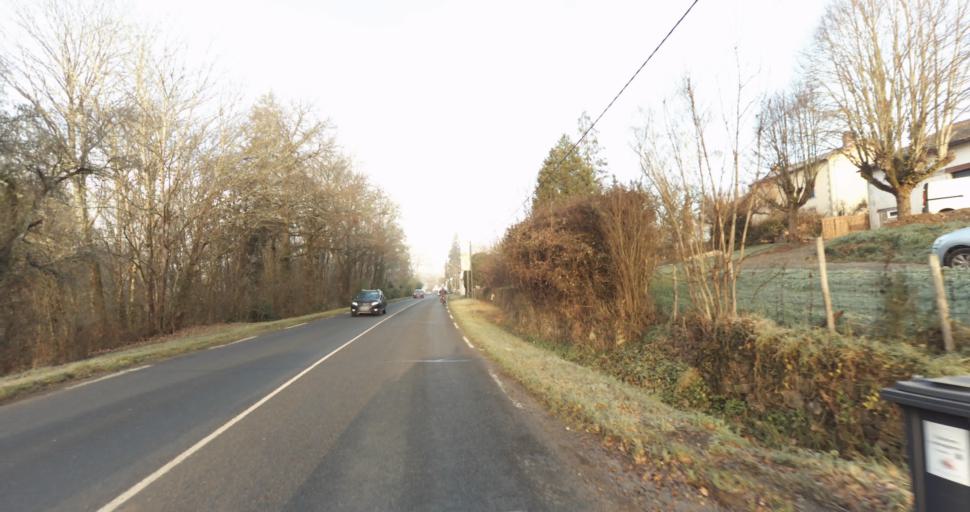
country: FR
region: Limousin
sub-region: Departement de la Haute-Vienne
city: Aixe-sur-Vienne
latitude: 45.7925
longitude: 1.1549
